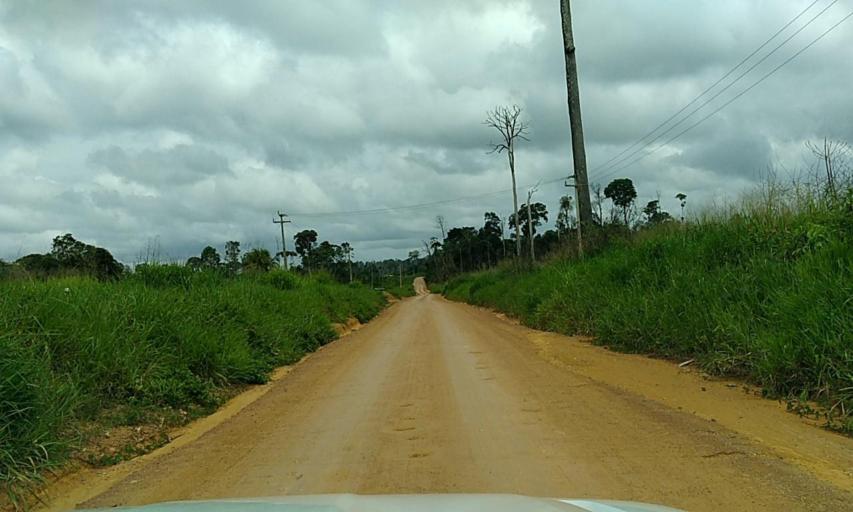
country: BR
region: Para
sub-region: Senador Jose Porfirio
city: Senador Jose Porfirio
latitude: -2.7692
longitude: -51.7822
